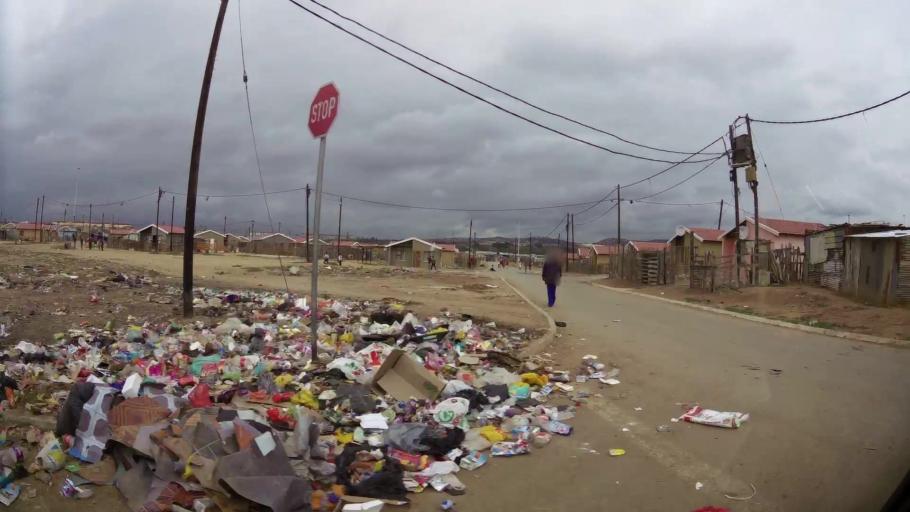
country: ZA
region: Eastern Cape
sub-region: Nelson Mandela Bay Metropolitan Municipality
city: Port Elizabeth
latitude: -33.8842
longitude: 25.5532
